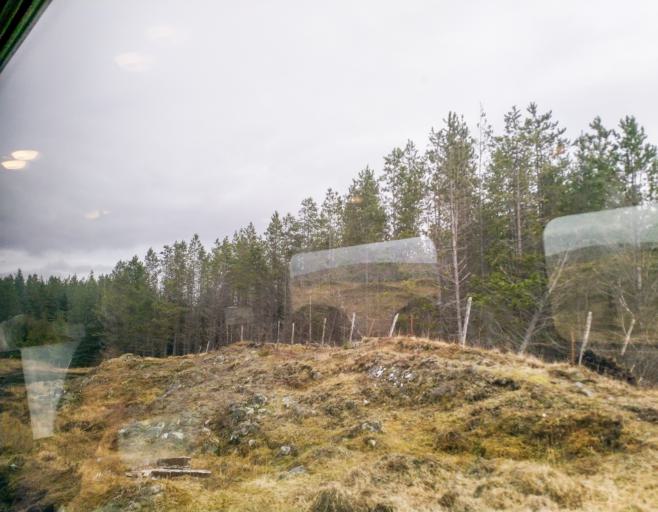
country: GB
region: Scotland
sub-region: Highland
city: Spean Bridge
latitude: 56.6527
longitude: -4.5663
